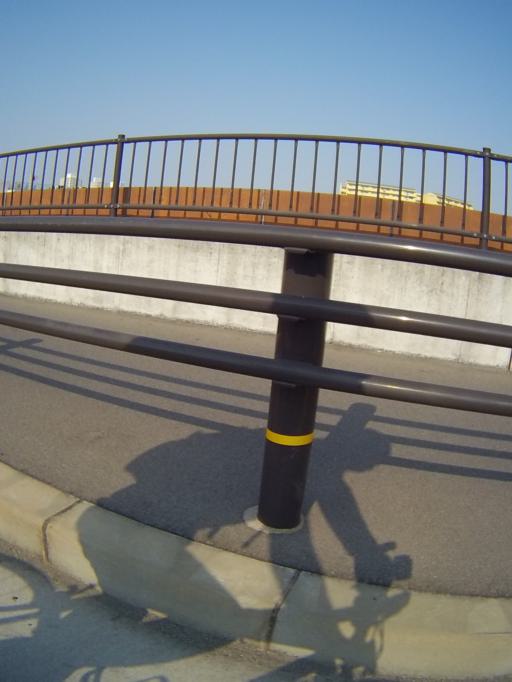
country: JP
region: Osaka
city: Osaka-shi
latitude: 34.6865
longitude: 135.4548
